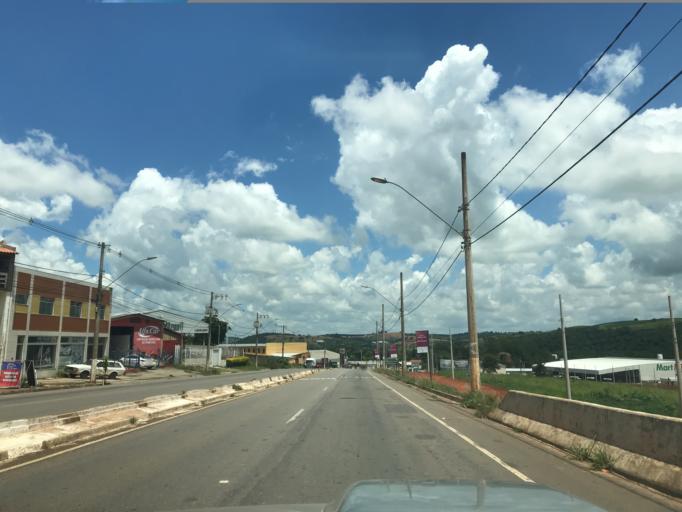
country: BR
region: Minas Gerais
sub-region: Tres Coracoes
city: Tres Coracoes
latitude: -21.6655
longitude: -45.2772
